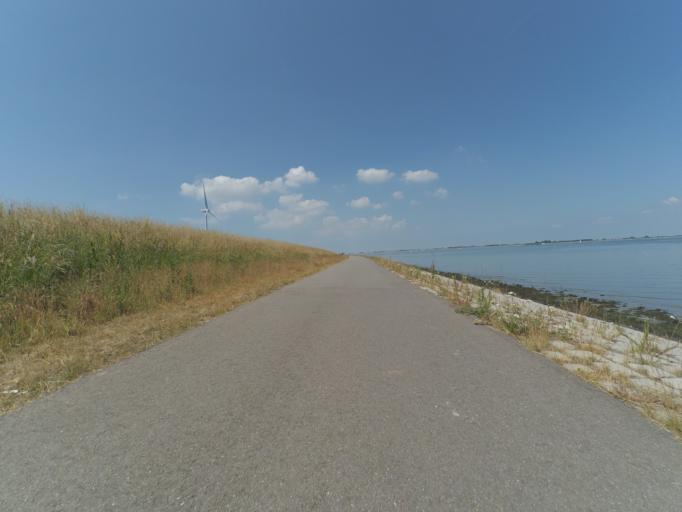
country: NL
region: Zeeland
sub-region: Schouwen-Duiveland
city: Bruinisse
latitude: 51.6119
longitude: 4.0821
